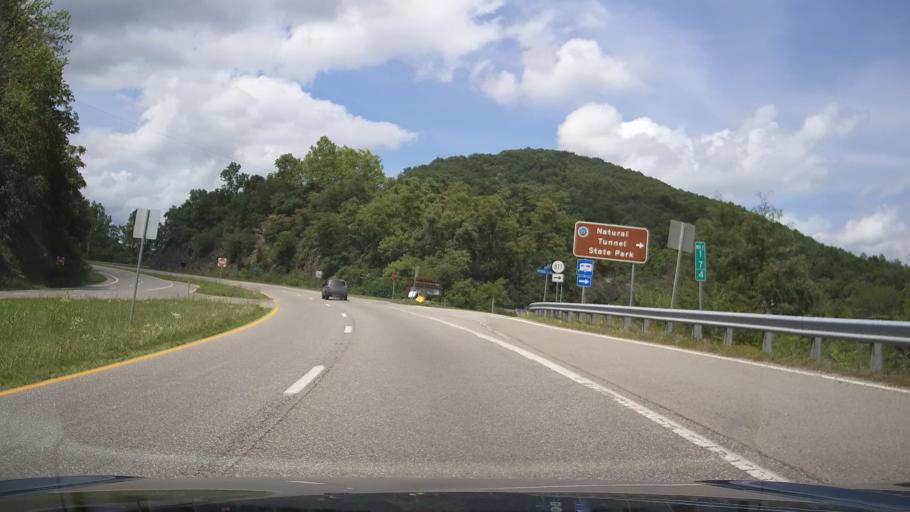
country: US
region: Tennessee
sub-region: Hawkins County
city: Mount Carmel
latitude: 36.6851
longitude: -82.7536
